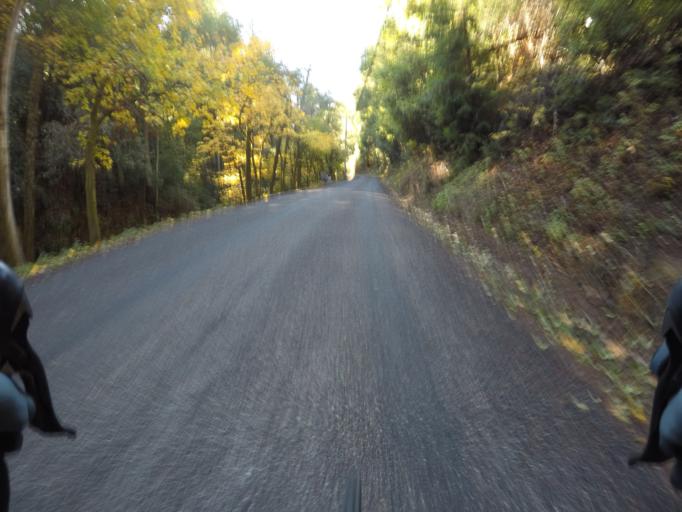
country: US
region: California
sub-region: Santa Cruz County
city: Lompico
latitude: 37.1034
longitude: -122.0297
